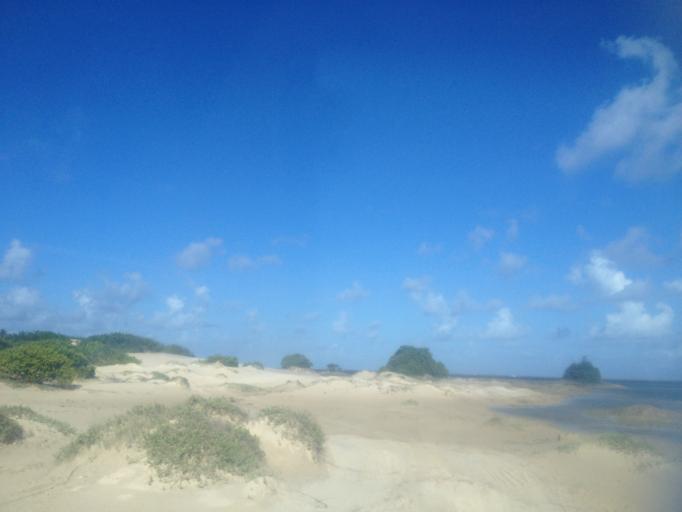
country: BR
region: Sergipe
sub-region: Indiaroba
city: Indiaroba
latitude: -11.4753
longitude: -37.3697
